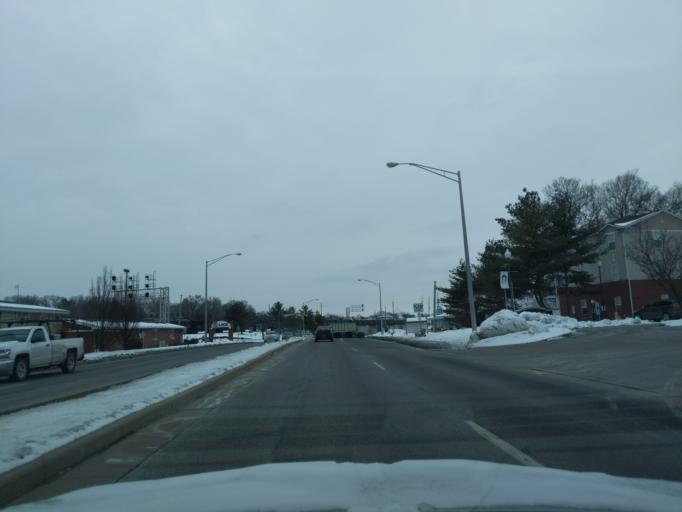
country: US
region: Indiana
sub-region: Tippecanoe County
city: Lafayette
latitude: 40.4362
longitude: -86.8863
